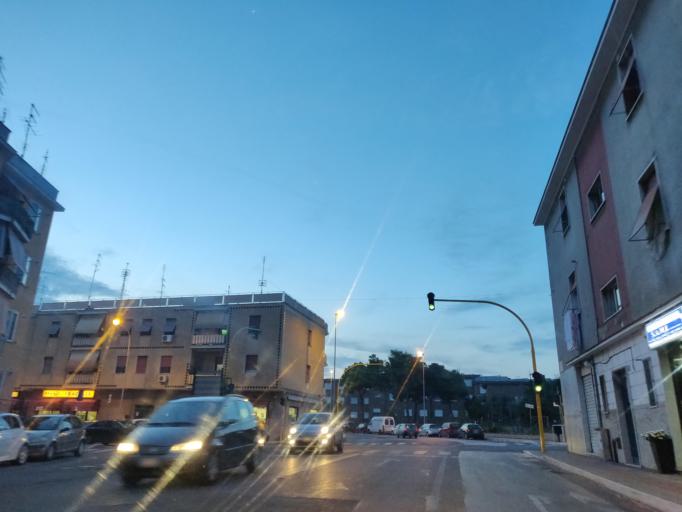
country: IT
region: Latium
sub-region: Citta metropolitana di Roma Capitale
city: Civitavecchia
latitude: 42.0940
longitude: 11.8059
